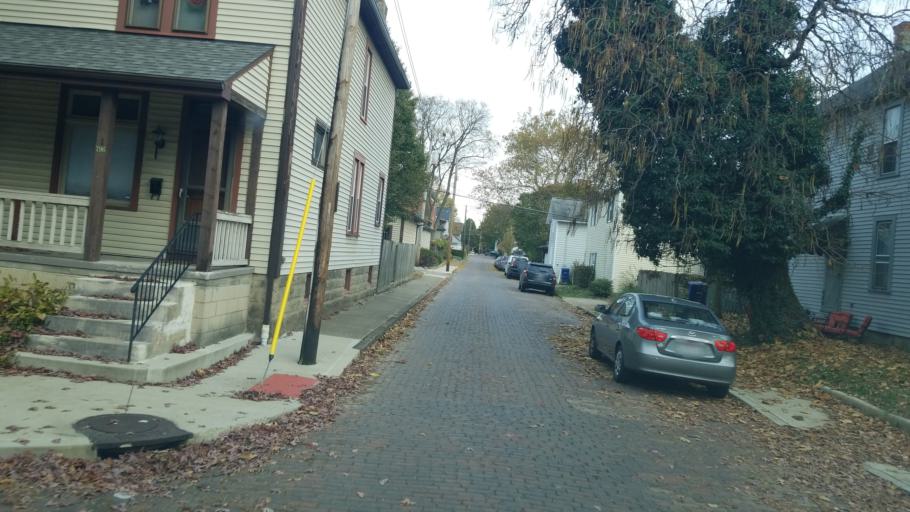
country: US
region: Ohio
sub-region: Franklin County
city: Columbus
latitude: 39.9469
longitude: -82.9884
